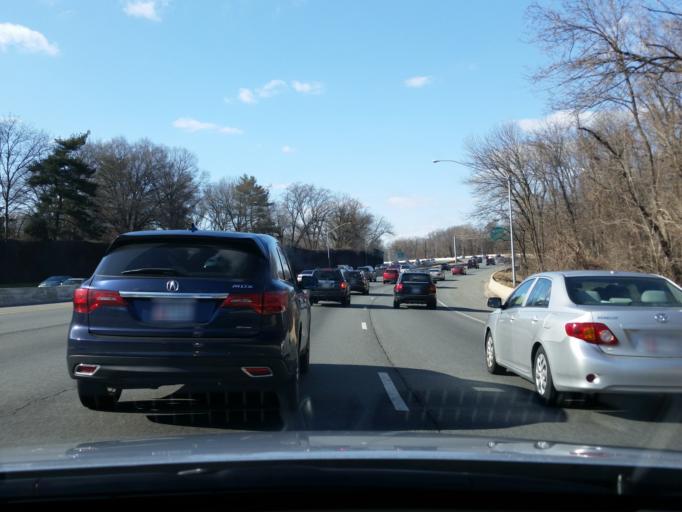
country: US
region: Maryland
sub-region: Montgomery County
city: South Kensington
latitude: 39.0078
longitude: -77.0869
